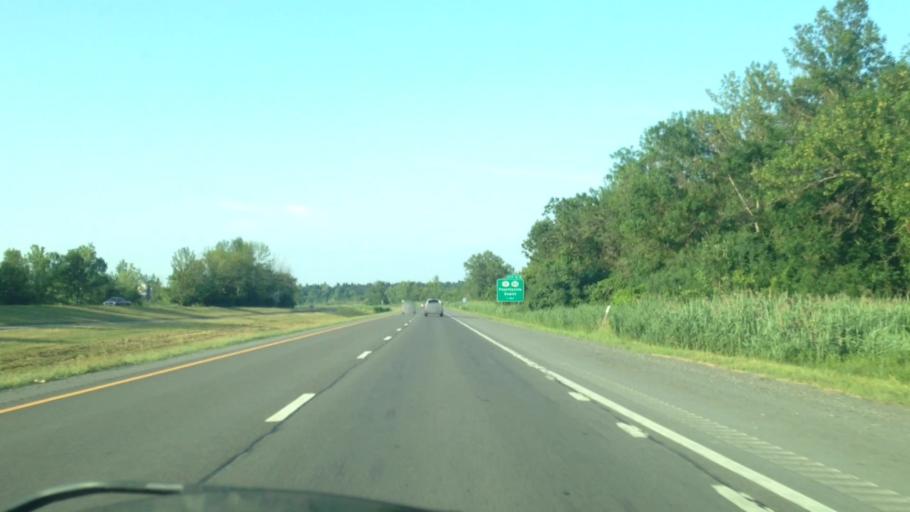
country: US
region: New York
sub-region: Onondaga County
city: East Syracuse
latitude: 43.0150
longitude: -76.0683
